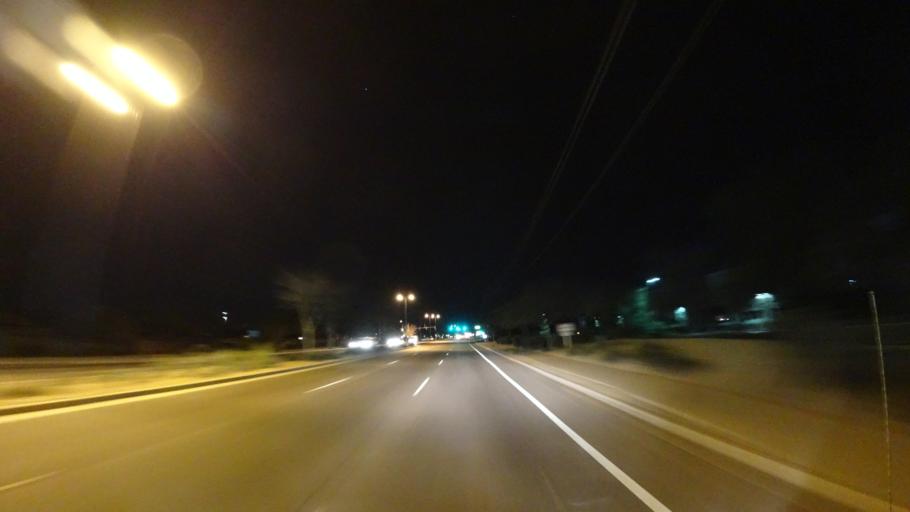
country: US
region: Arizona
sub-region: Maricopa County
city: San Carlos
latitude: 33.3567
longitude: -111.8246
